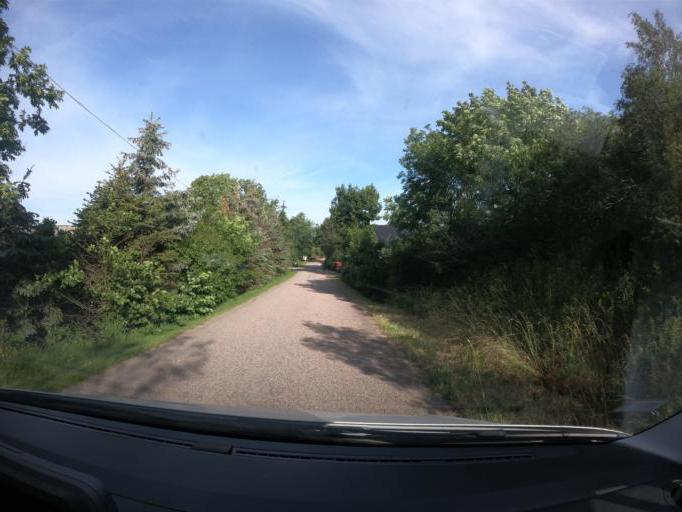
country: SE
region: Skane
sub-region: Bastads Kommun
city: Forslov
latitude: 56.3447
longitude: 12.8089
